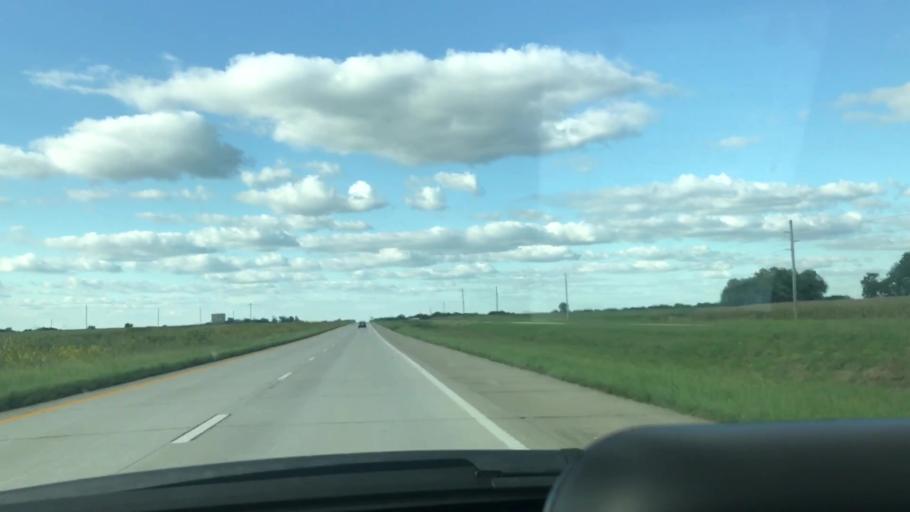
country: US
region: Missouri
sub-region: Benton County
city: Cole Camp
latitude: 38.5118
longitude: -93.2727
